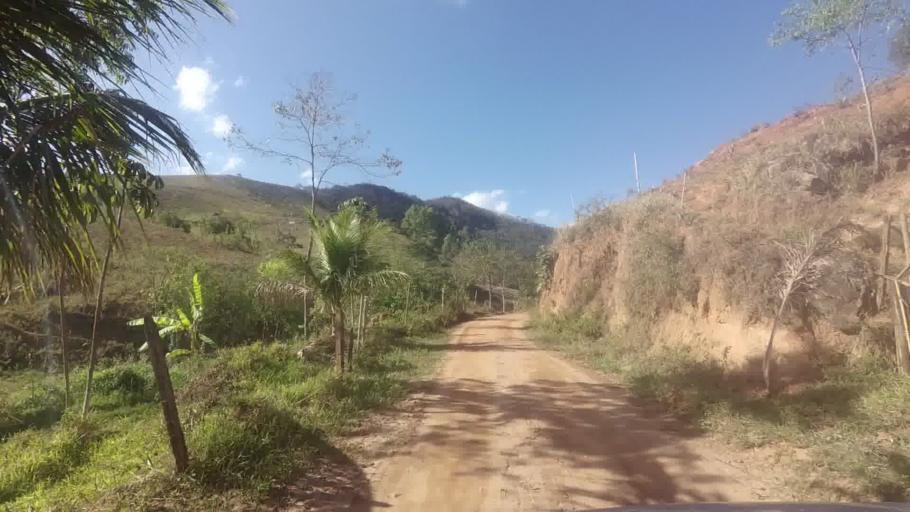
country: BR
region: Espirito Santo
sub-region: Sao Jose Do Calcado
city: Sao Jose do Calcado
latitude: -21.0360
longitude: -41.5996
